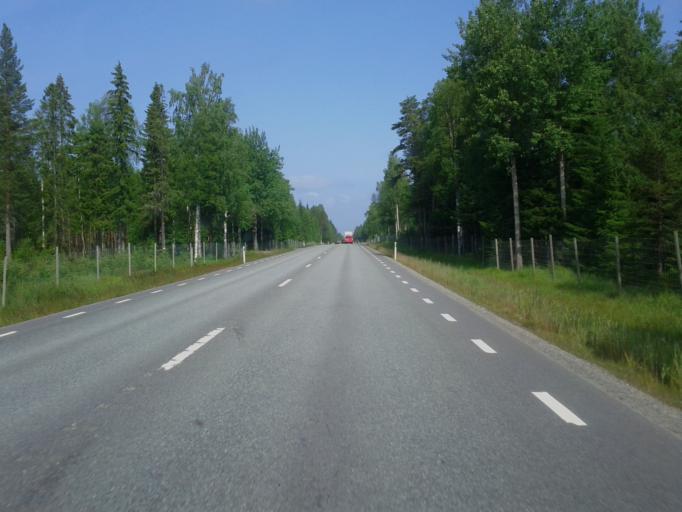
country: SE
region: Vaesterbotten
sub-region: Skelleftea Kommun
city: Burea
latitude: 64.5708
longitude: 21.2259
